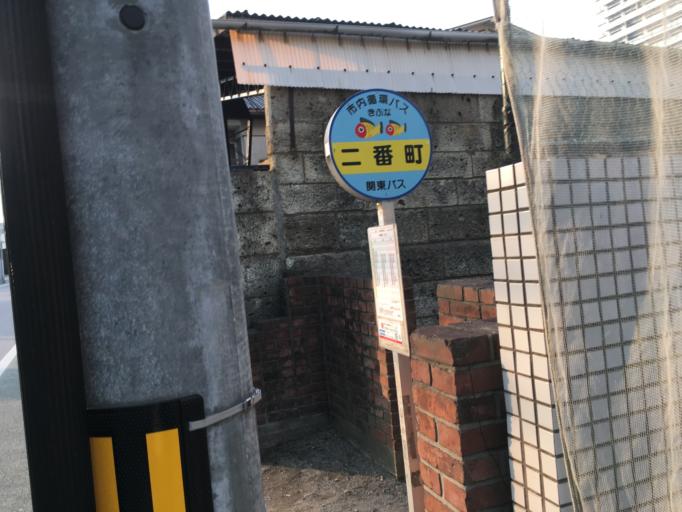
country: JP
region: Tochigi
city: Utsunomiya-shi
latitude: 36.5592
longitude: 139.8890
